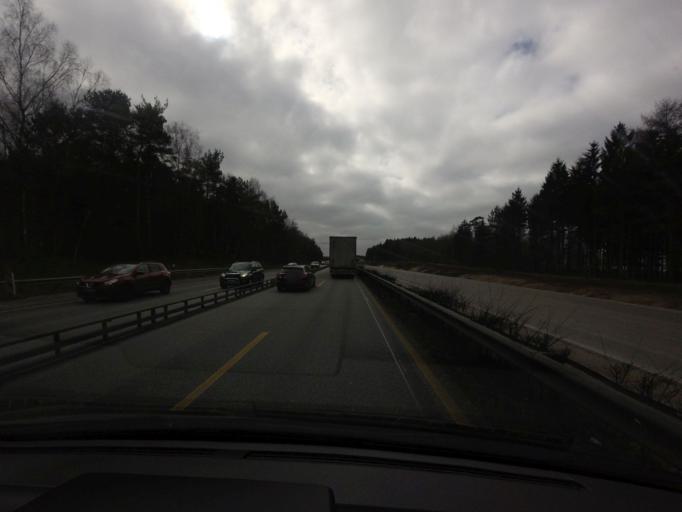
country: DE
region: Schleswig-Holstein
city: Nutzen
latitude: 53.8382
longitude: 9.9277
